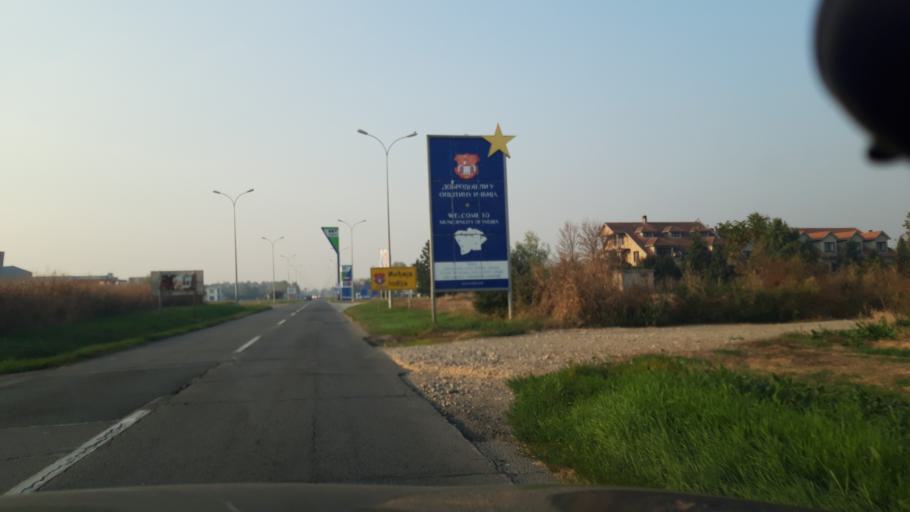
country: RS
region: Autonomna Pokrajina Vojvodina
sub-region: Sremski Okrug
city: Ingija
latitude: 45.0251
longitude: 20.1070
